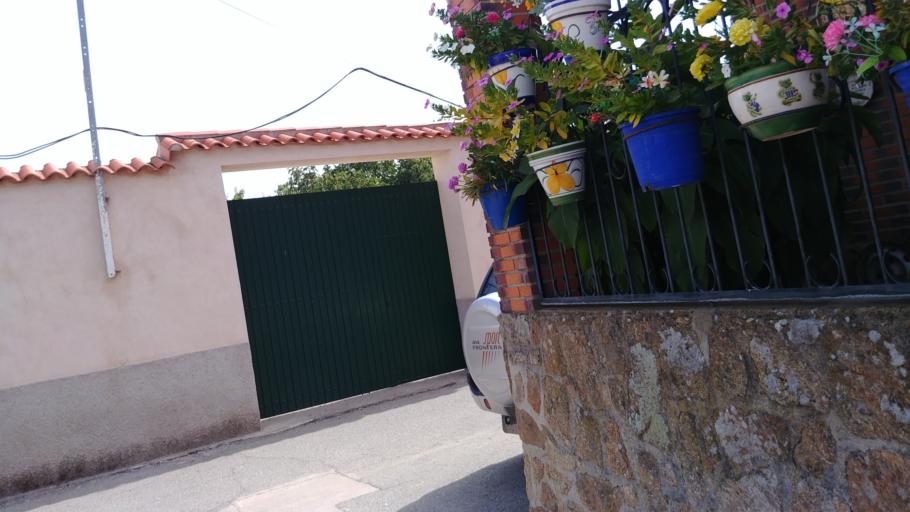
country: ES
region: Castille-La Mancha
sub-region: Province of Toledo
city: Navalcan
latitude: 40.0672
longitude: -5.0957
